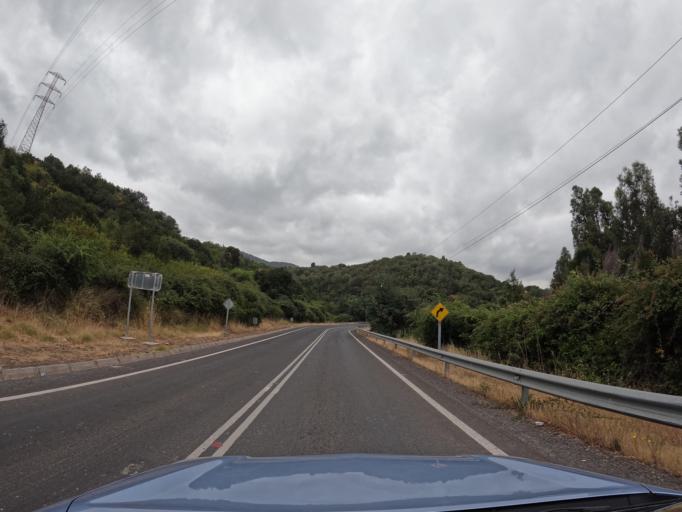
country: CL
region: O'Higgins
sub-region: Provincia de Colchagua
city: Chimbarongo
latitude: -34.7276
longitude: -71.0945
